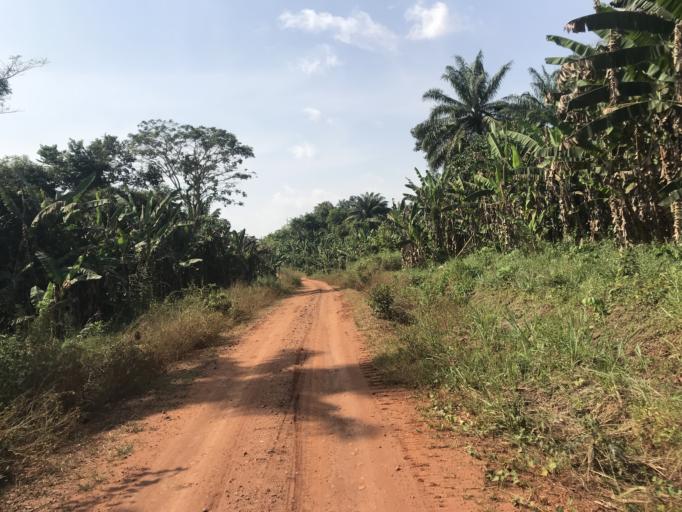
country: NG
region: Osun
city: Ilesa
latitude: 7.6307
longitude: 4.6815
